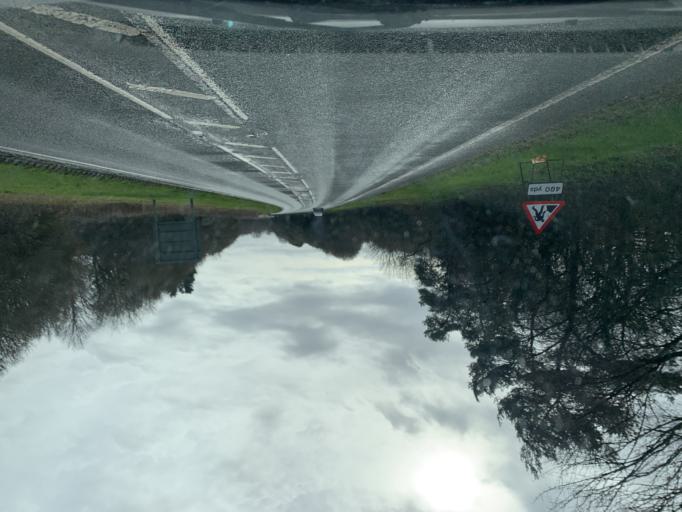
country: GB
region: England
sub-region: Hampshire
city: Fordingbridge
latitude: 50.9352
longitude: -1.7849
